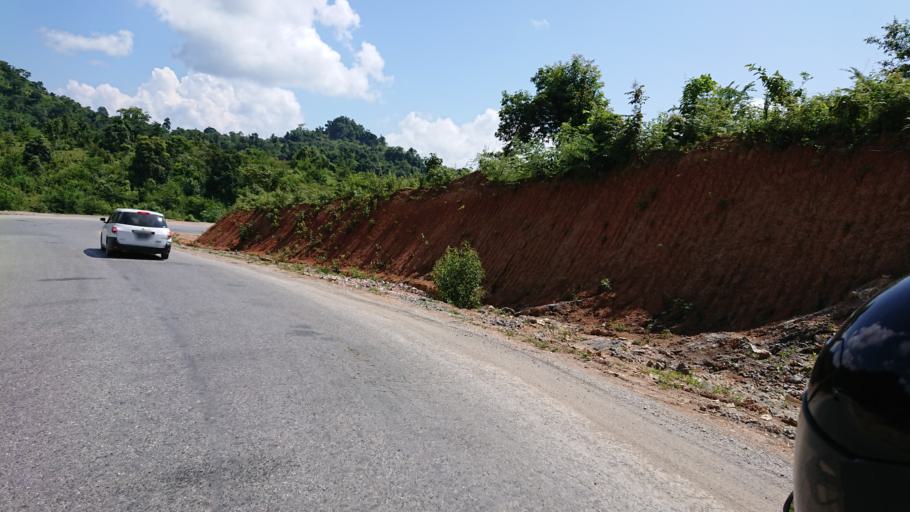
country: MM
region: Shan
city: Taunggyi
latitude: 20.8177
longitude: 97.3139
